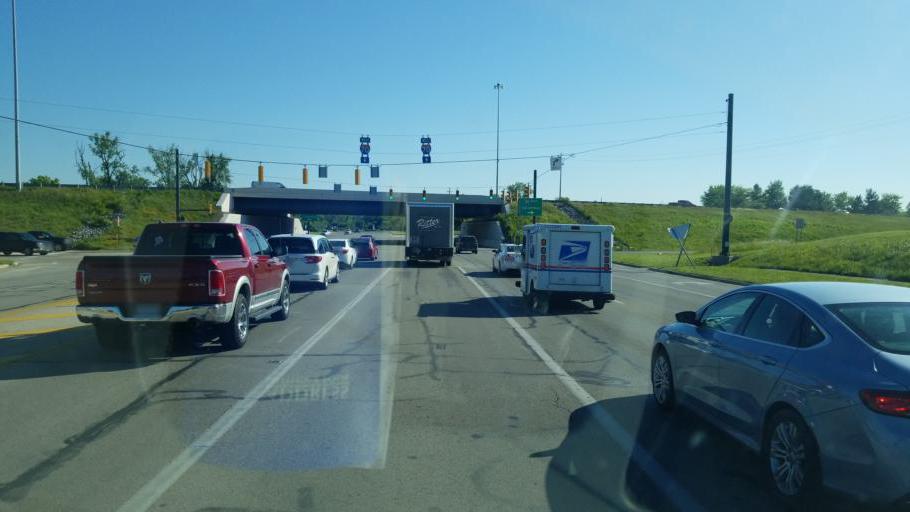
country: US
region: Ohio
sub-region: Montgomery County
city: Huber Heights
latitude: 39.8667
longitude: -84.1010
